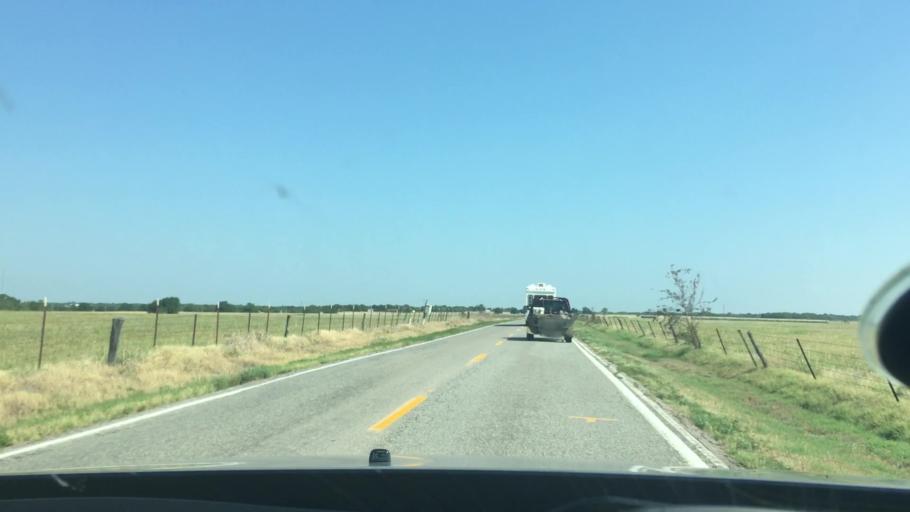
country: US
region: Oklahoma
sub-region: Johnston County
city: Tishomingo
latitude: 34.1674
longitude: -96.5091
